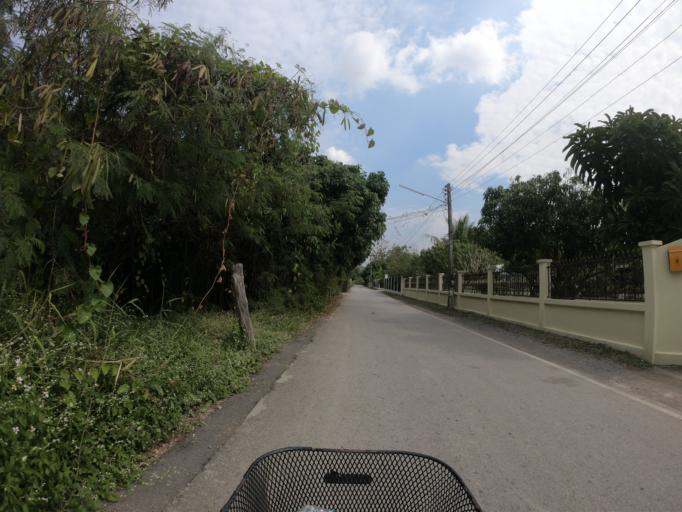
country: TH
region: Chiang Mai
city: Saraphi
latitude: 18.7081
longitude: 99.0348
